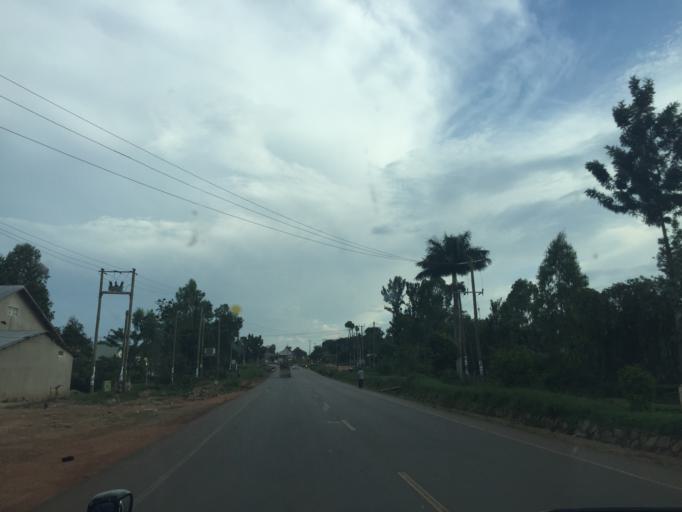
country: UG
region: Central Region
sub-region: Luwero District
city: Luwero
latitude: 0.8548
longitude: 32.4866
